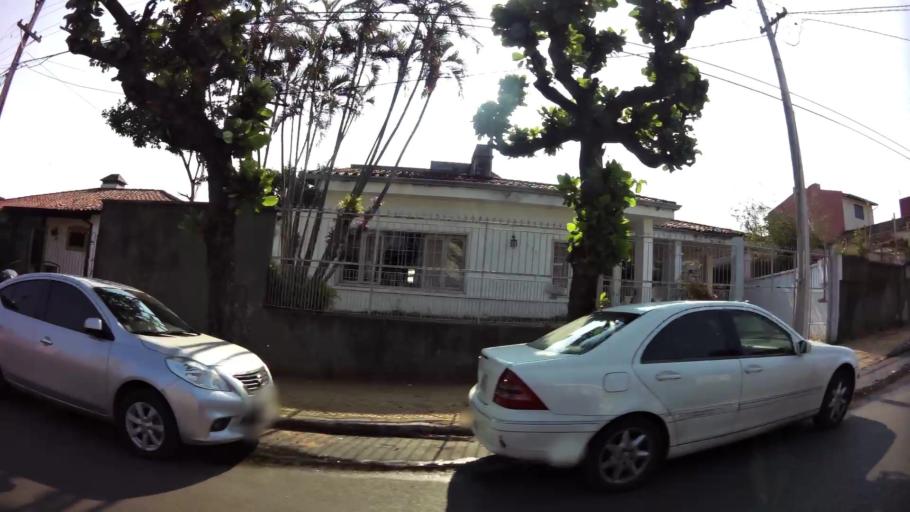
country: PY
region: Asuncion
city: Asuncion
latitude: -25.3054
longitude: -57.6301
